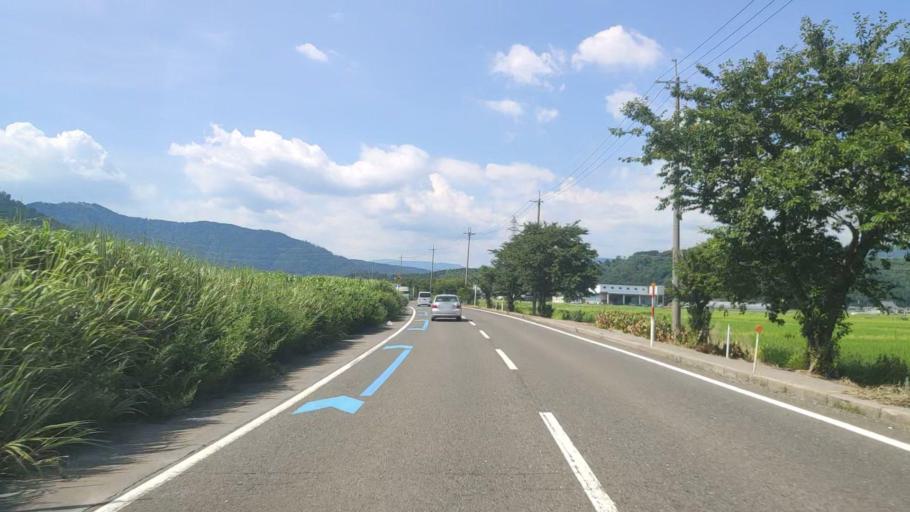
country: JP
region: Shiga Prefecture
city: Nagahama
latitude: 35.4815
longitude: 136.2095
